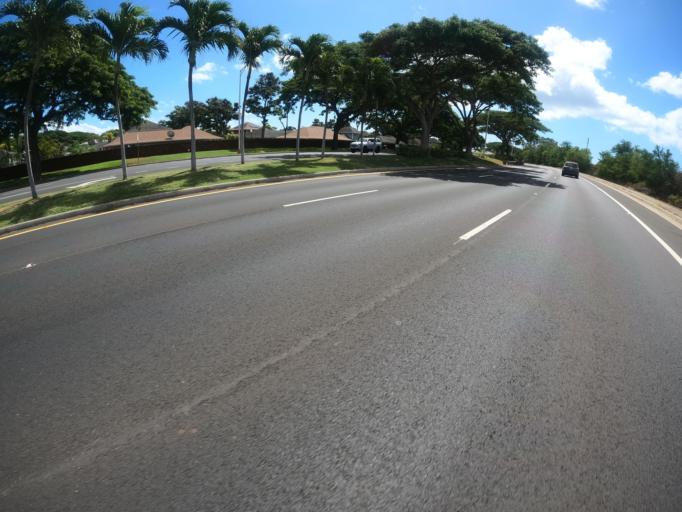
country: US
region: Hawaii
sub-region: Honolulu County
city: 'Ewa Gentry
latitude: 21.3591
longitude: -158.0297
